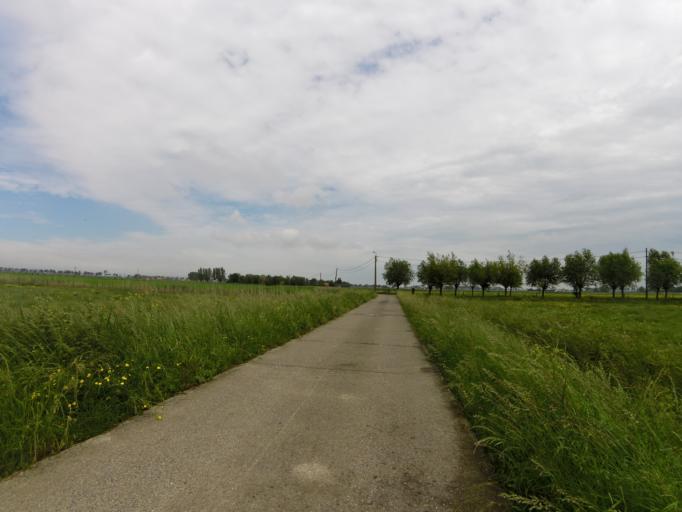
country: BE
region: Flanders
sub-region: Provincie West-Vlaanderen
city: Middelkerke
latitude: 51.1493
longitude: 2.8274
